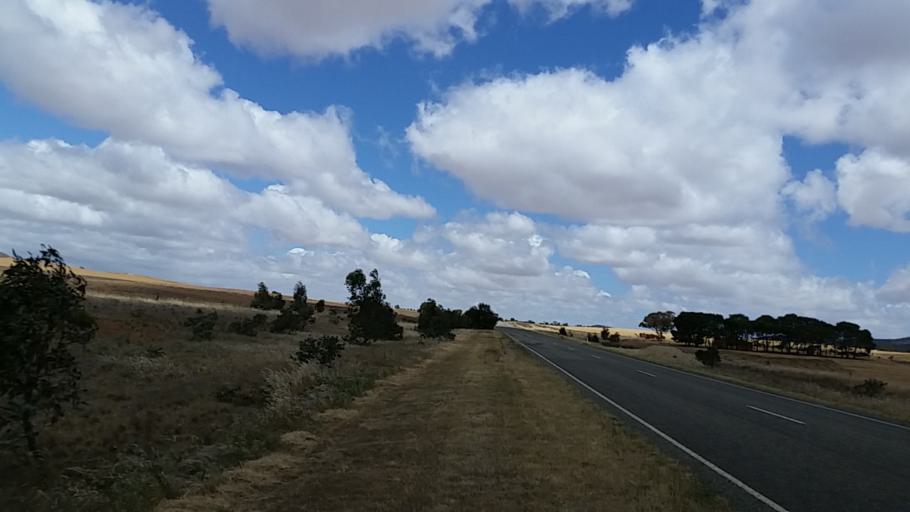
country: AU
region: South Australia
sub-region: Peterborough
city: Peterborough
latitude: -32.8638
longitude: 138.5406
